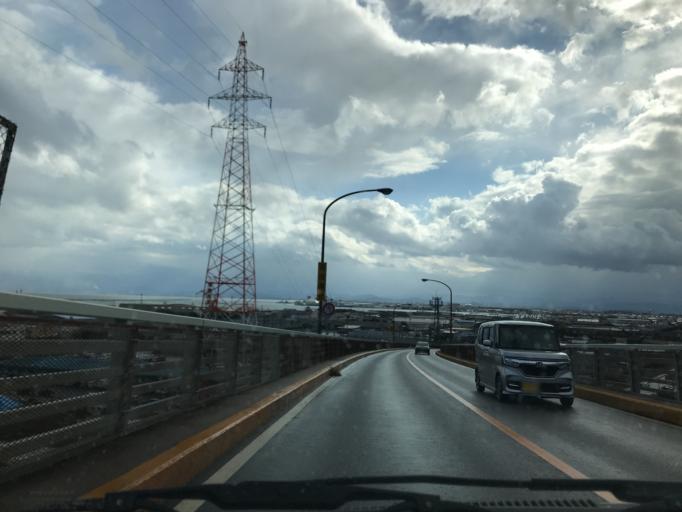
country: JP
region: Shimane
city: Sakaiminato
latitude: 35.5471
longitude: 133.2454
